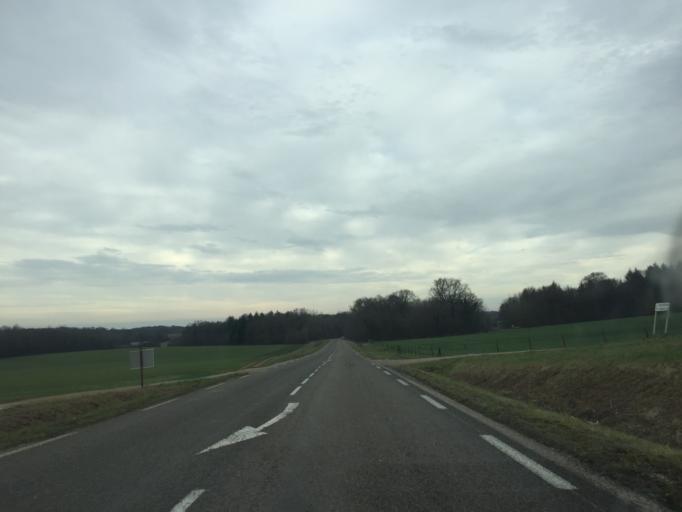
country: FR
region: Franche-Comte
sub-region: Departement du Jura
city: Poligny
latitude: 46.8409
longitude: 5.5720
